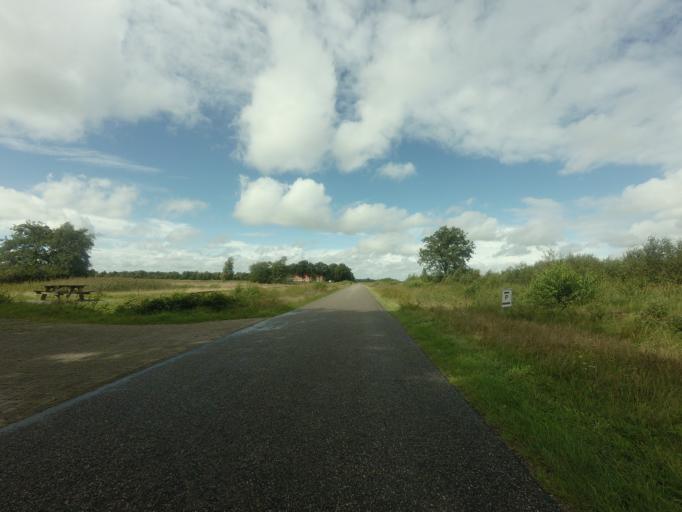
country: NL
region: Groningen
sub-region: Gemeente Leek
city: Leek
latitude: 53.0028
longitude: 6.3718
